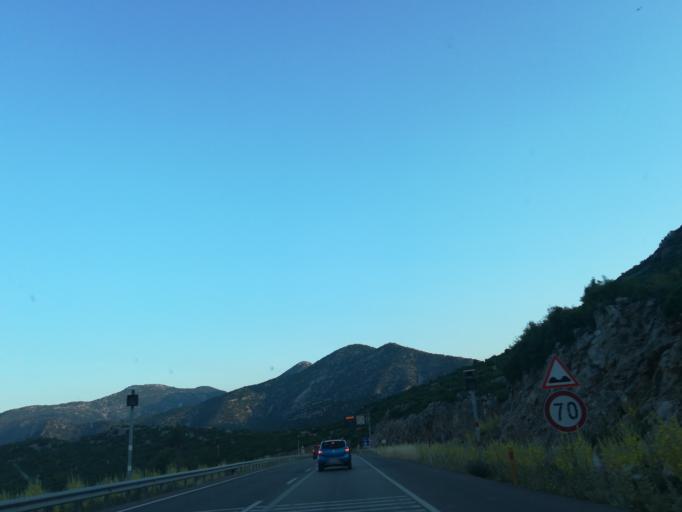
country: TR
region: Antalya
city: Dagbeli
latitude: 37.1594
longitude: 30.5015
